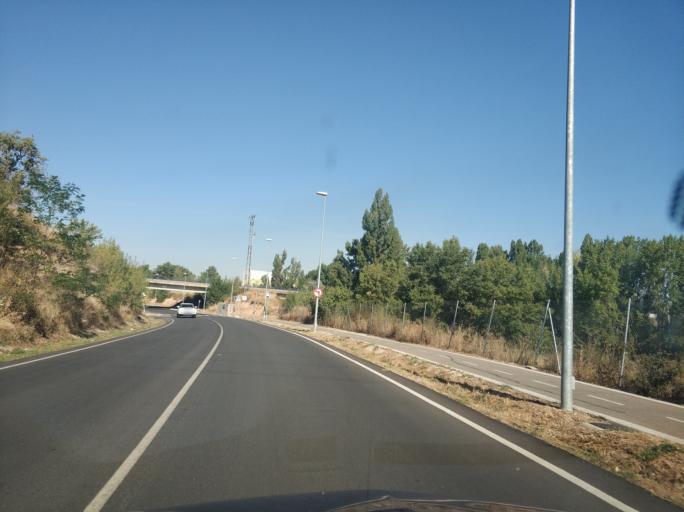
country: ES
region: Castille and Leon
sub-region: Provincia de Burgos
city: Aranda de Duero
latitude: 41.6726
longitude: -3.6954
